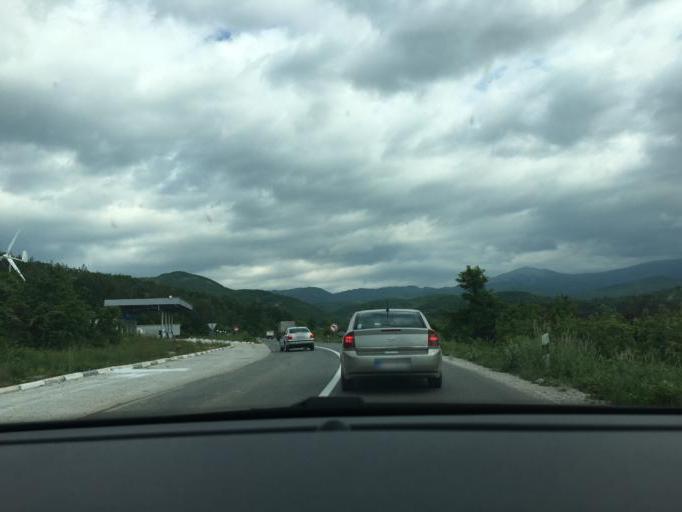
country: MK
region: Resen
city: Jankovec
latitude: 41.1215
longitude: 21.0092
